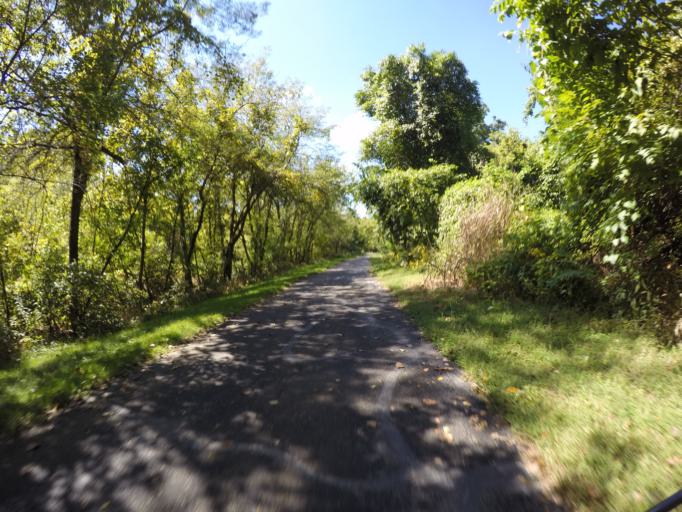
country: US
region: Kansas
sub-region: Johnson County
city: Lenexa
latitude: 38.9123
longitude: -94.7202
